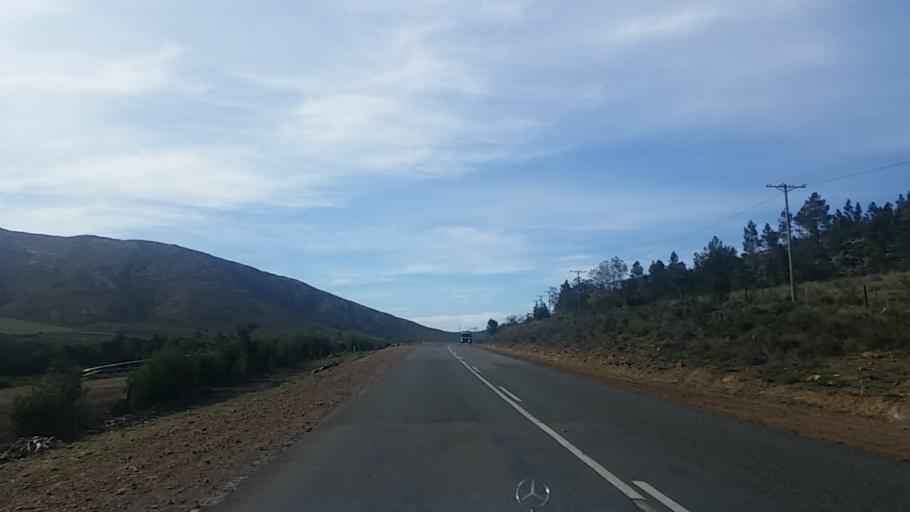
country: ZA
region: Western Cape
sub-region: Eden District Municipality
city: George
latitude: -33.8376
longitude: 22.3489
